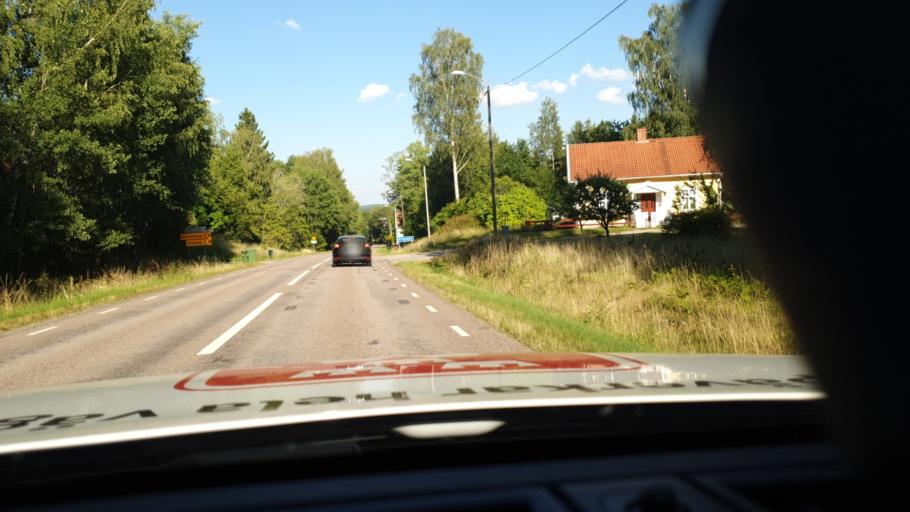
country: SE
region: OEstergoetland
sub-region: Ydre Kommun
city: OEsterbymo
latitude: 57.7992
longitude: 15.1345
